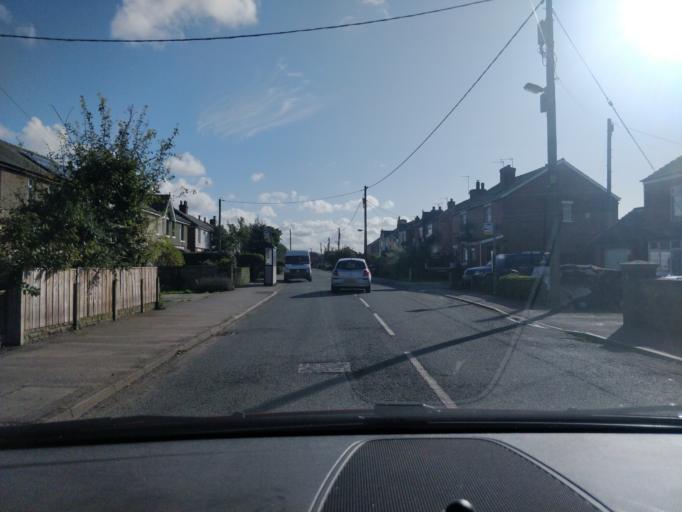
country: GB
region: England
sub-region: Lancashire
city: Banks
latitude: 53.6871
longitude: -2.9138
